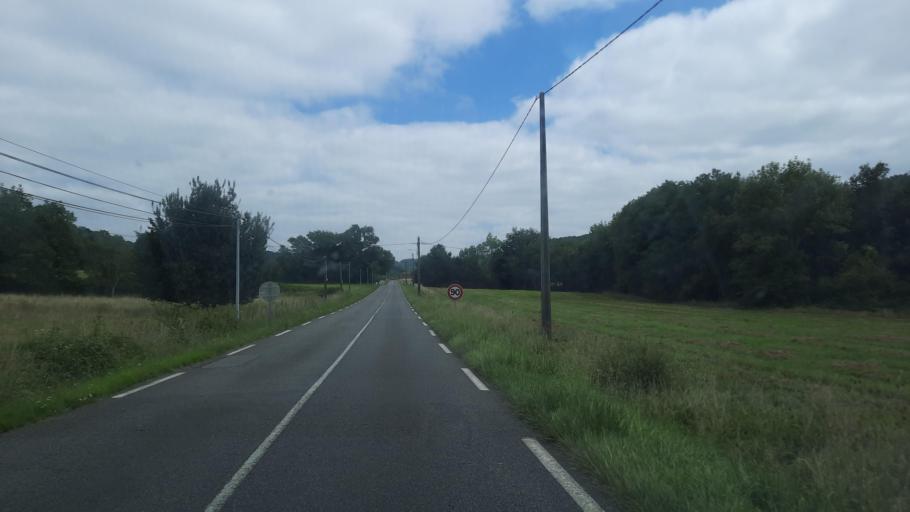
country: FR
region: Midi-Pyrenees
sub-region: Departement des Hautes-Pyrenees
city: Tournay
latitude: 43.3060
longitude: 0.2421
